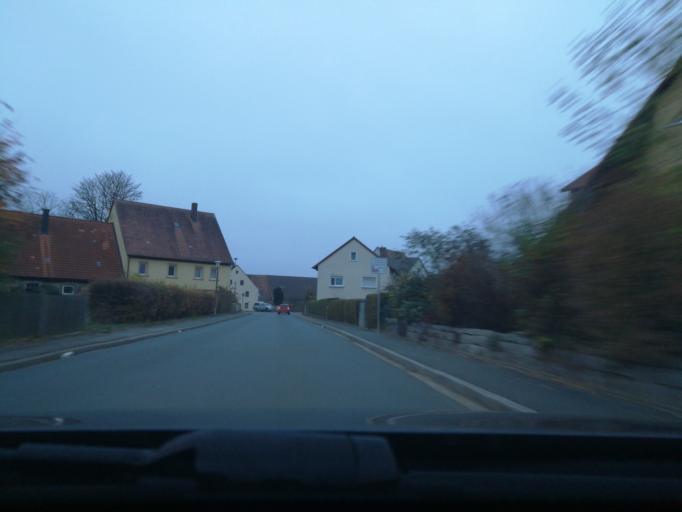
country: DE
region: Bavaria
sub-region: Regierungsbezirk Mittelfranken
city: Obermichelbach
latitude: 49.5141
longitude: 10.9264
